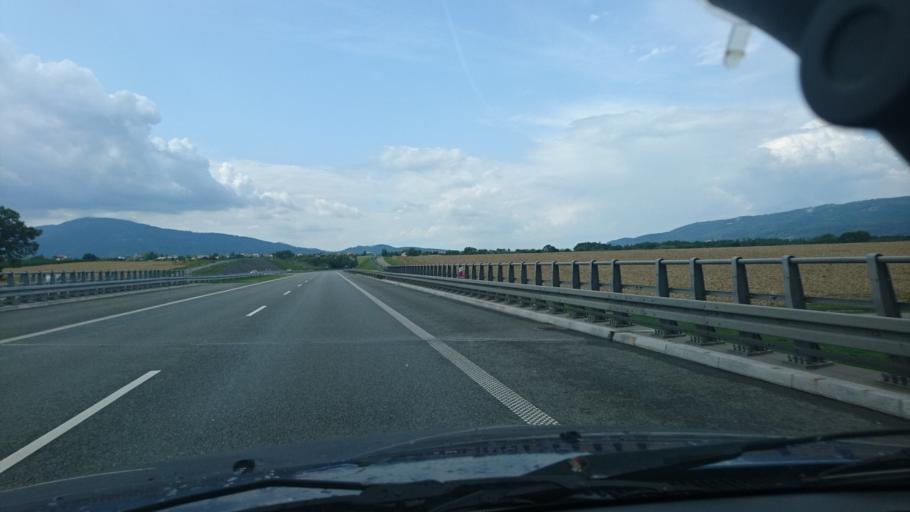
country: PL
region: Silesian Voivodeship
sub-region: Powiat zywiecki
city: Lodygowice
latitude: 49.7020
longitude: 19.1266
